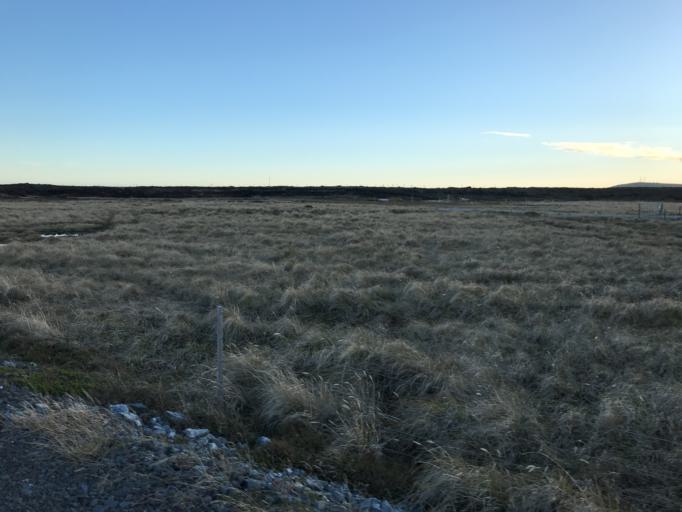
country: FK
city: Stanley
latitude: -51.7012
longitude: -57.8423
